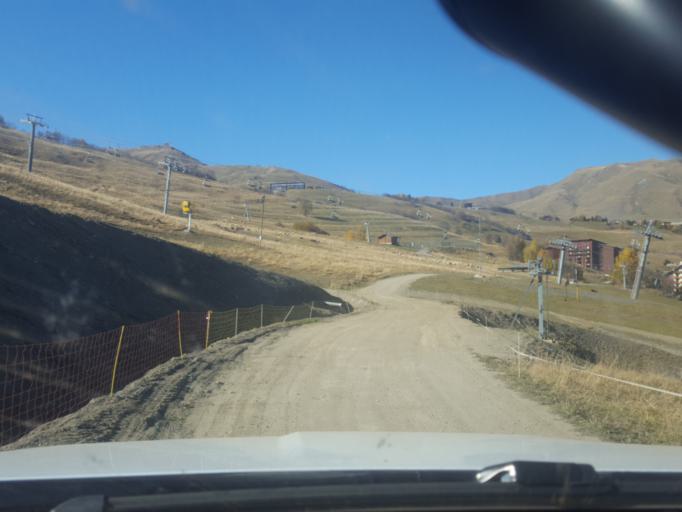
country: FR
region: Rhone-Alpes
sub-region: Departement de la Savoie
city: Saint-Jean-de-Maurienne
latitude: 45.2389
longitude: 6.2669
